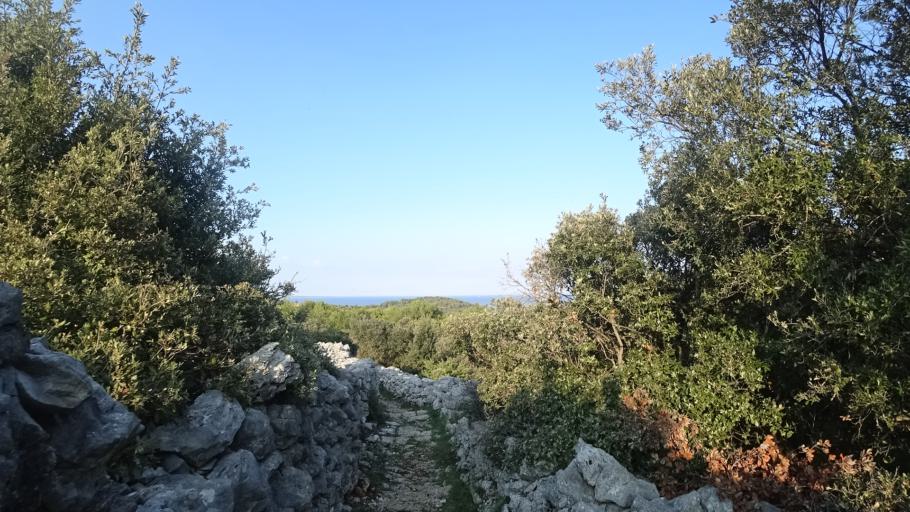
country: HR
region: Primorsko-Goranska
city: Mali Losinj
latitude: 44.5245
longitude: 14.4759
